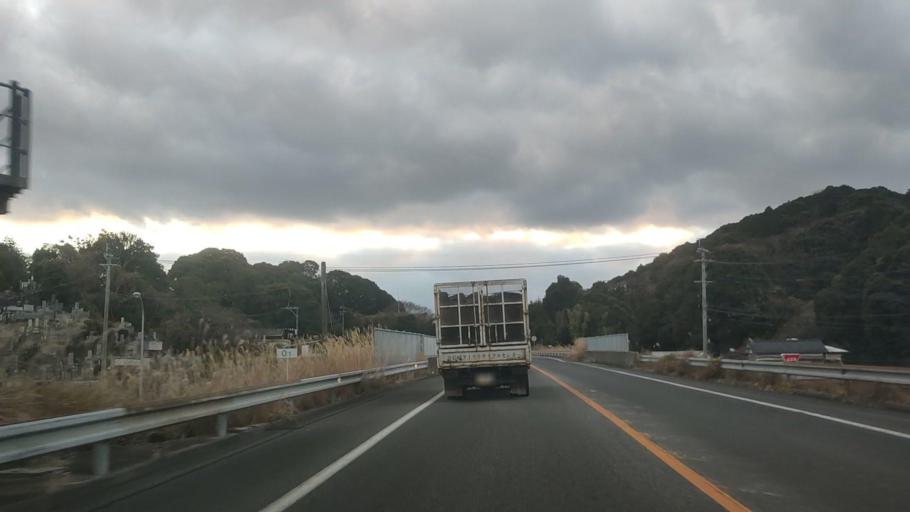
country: JP
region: Nagasaki
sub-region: Isahaya-shi
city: Isahaya
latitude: 32.8164
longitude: 129.9661
